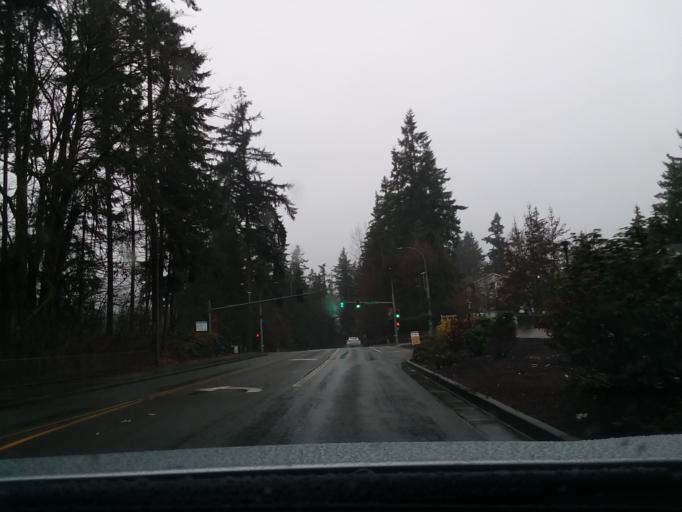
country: US
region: Washington
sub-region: Snohomish County
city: Mill Creek
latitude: 47.8756
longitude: -122.2176
